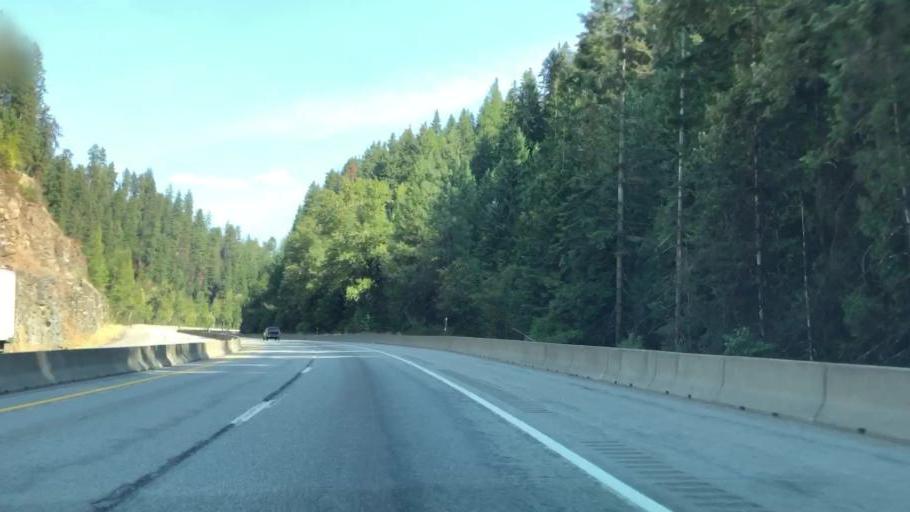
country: US
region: Idaho
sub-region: Kootenai County
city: Coeur d'Alene
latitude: 47.6245
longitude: -116.5672
